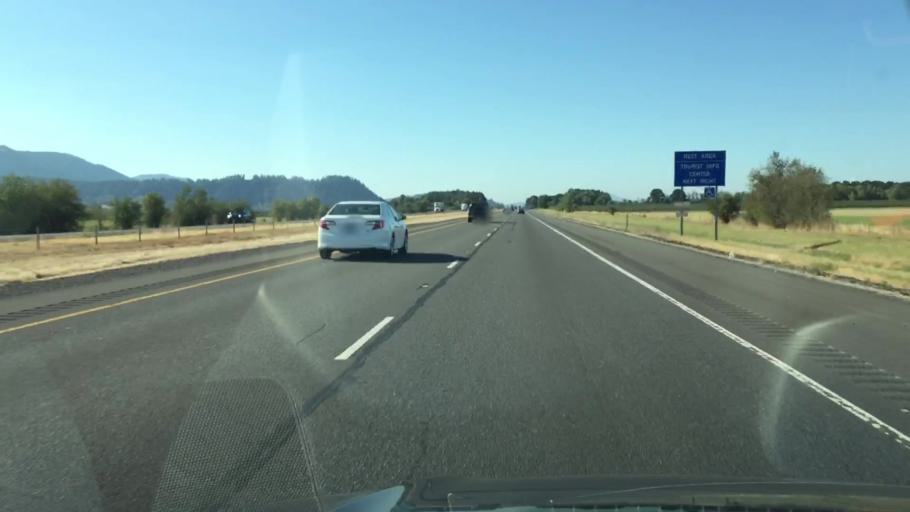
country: US
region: Oregon
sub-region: Lane County
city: Coburg
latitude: 44.2476
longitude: -123.0613
